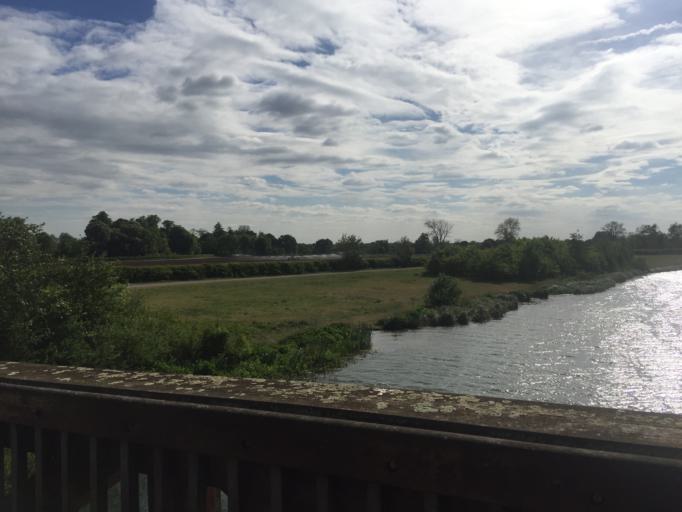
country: GB
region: England
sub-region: Royal Borough of Windsor and Maidenhead
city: Bray
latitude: 51.5065
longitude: -0.6668
